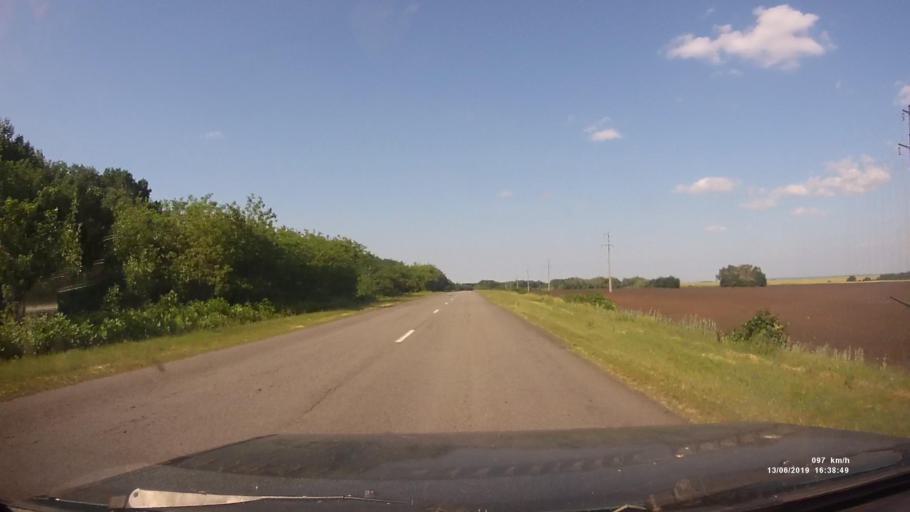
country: RU
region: Rostov
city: Kazanskaya
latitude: 49.9227
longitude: 41.3298
